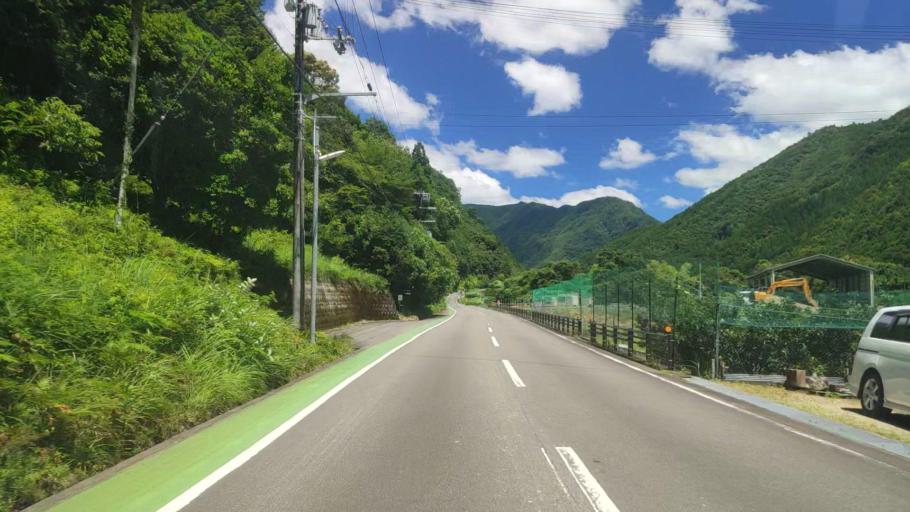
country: JP
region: Wakayama
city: Shingu
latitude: 33.9506
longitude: 135.9766
